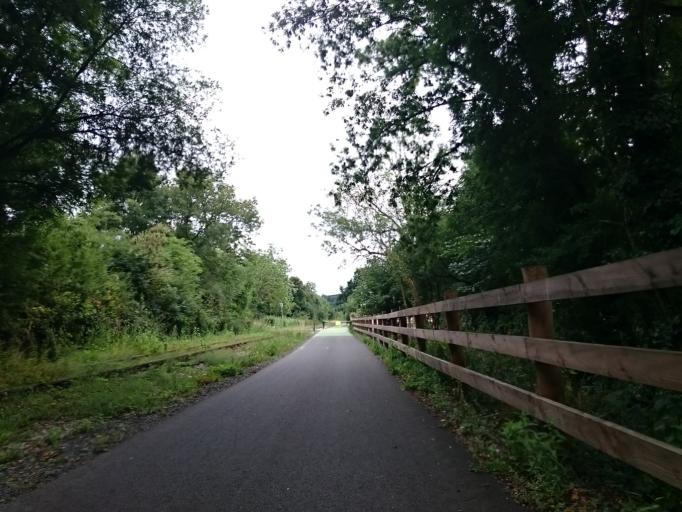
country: FR
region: Lower Normandy
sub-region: Departement du Calvados
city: Thury-Harcourt
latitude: 49.0175
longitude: -0.4675
